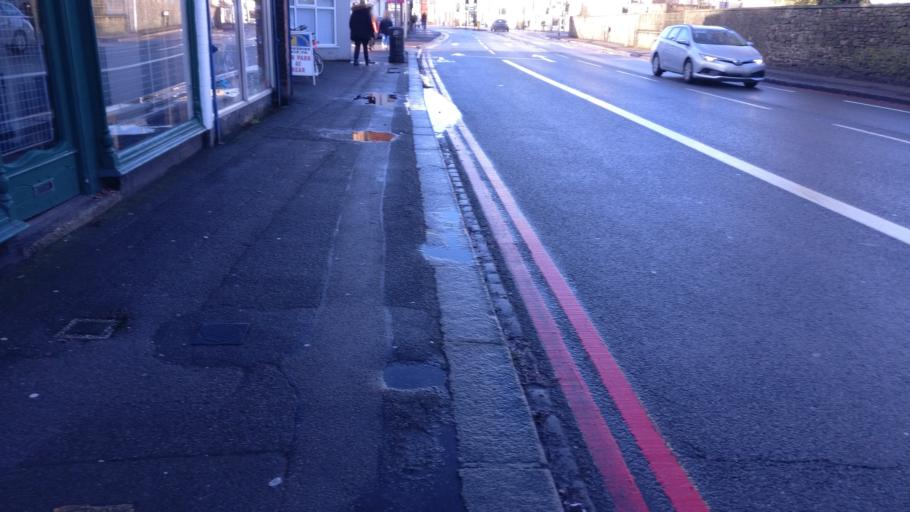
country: GB
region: England
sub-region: Reading
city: Reading
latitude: 51.4526
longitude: -0.9471
